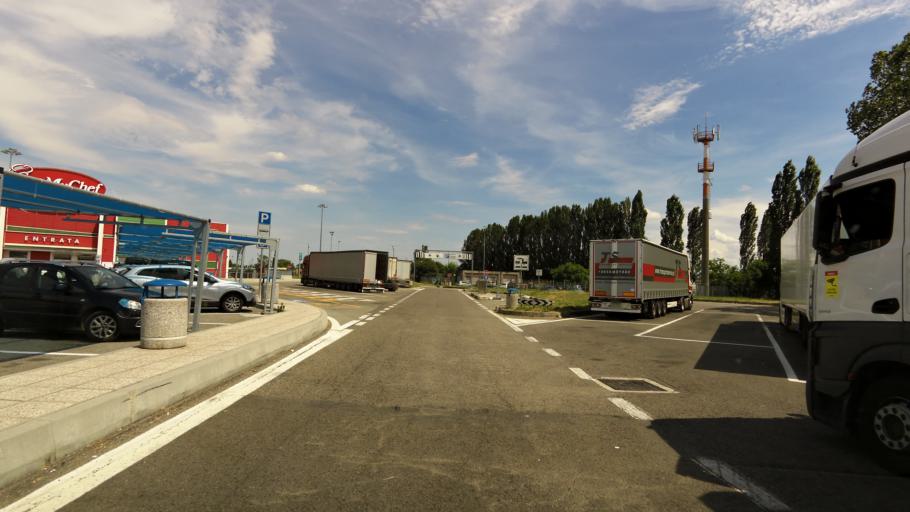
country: IT
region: Emilia-Romagna
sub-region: Provincia di Bologna
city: Anzola dell'Emilia
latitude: 44.5181
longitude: 11.2137
